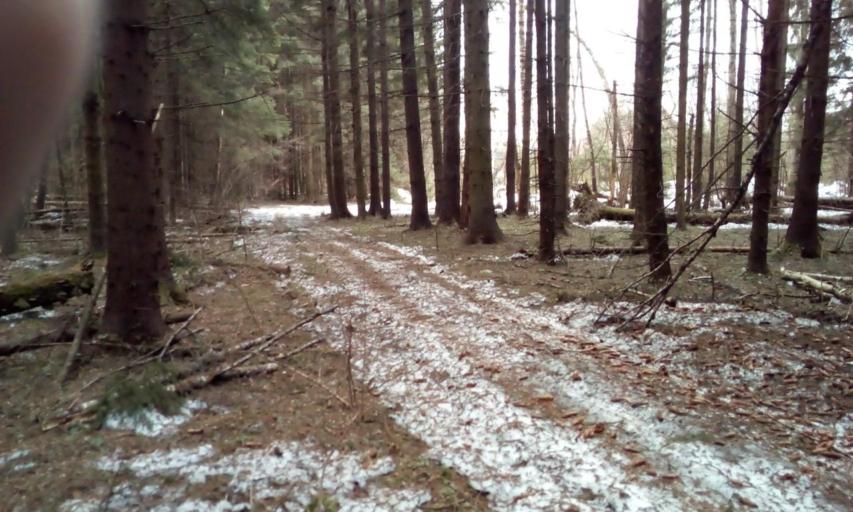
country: RU
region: Moskovskaya
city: Annino
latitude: 55.5438
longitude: 37.2415
